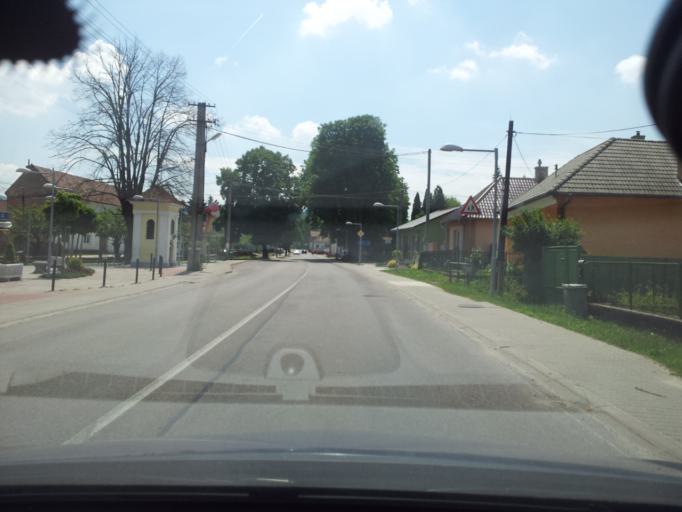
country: SK
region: Nitriansky
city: Partizanske
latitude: 48.6094
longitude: 18.4350
